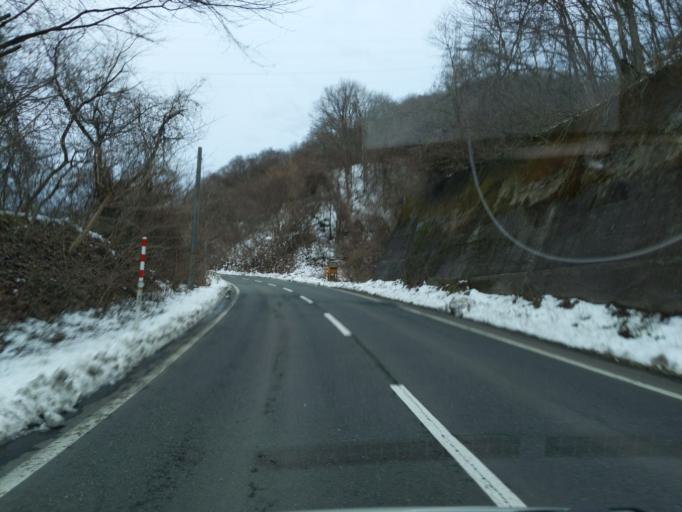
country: JP
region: Iwate
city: Mizusawa
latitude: 39.0992
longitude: 141.2658
